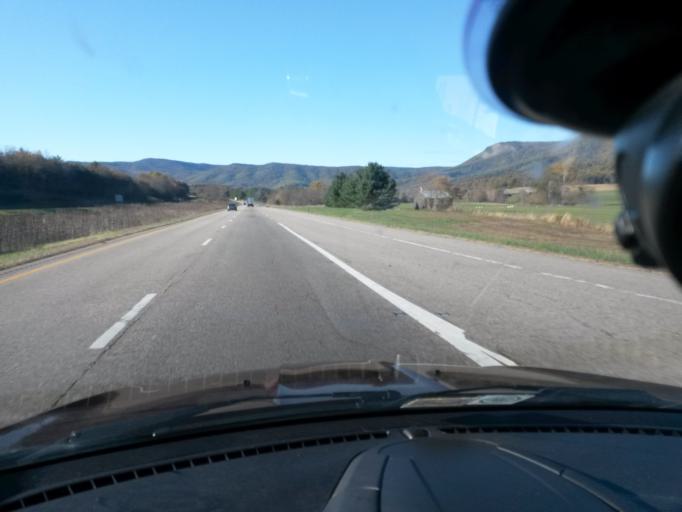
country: US
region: Virginia
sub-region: City of Lexington
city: Lexington
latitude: 37.8551
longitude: -79.4811
